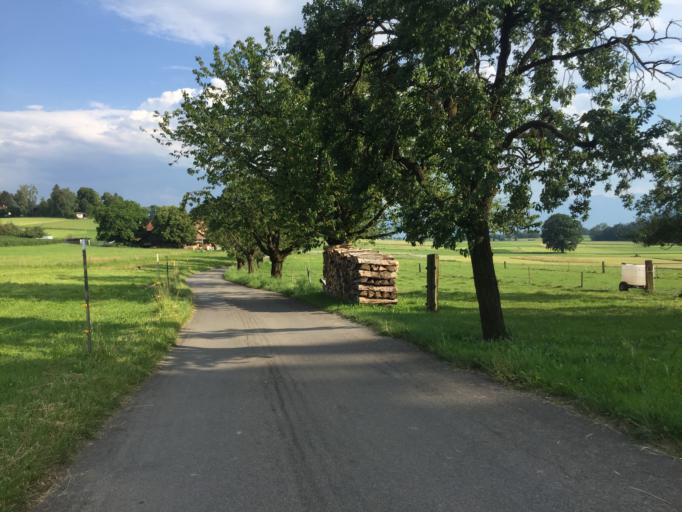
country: CH
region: Bern
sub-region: Bern-Mittelland District
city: Rubigen
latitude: 46.9013
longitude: 7.5704
